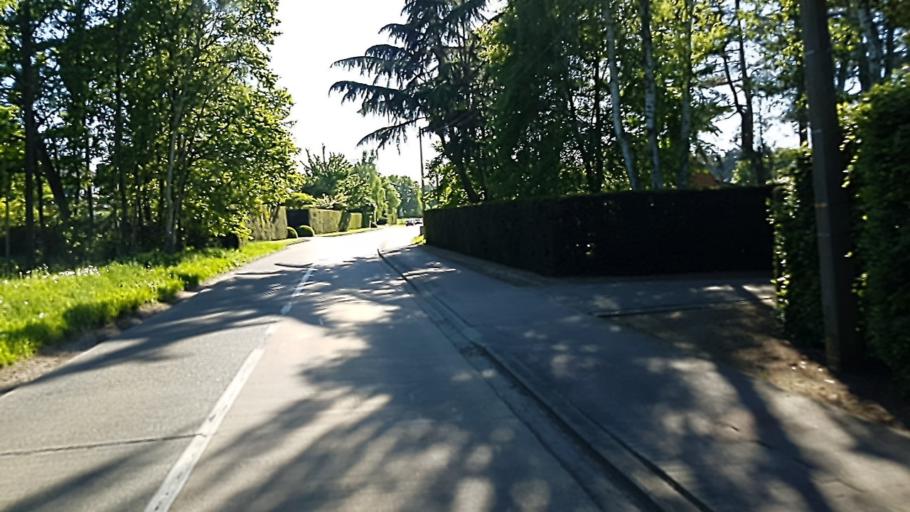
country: BE
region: Flanders
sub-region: Provincie Antwerpen
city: Heist-op-den-Berg
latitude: 51.0966
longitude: 4.7065
